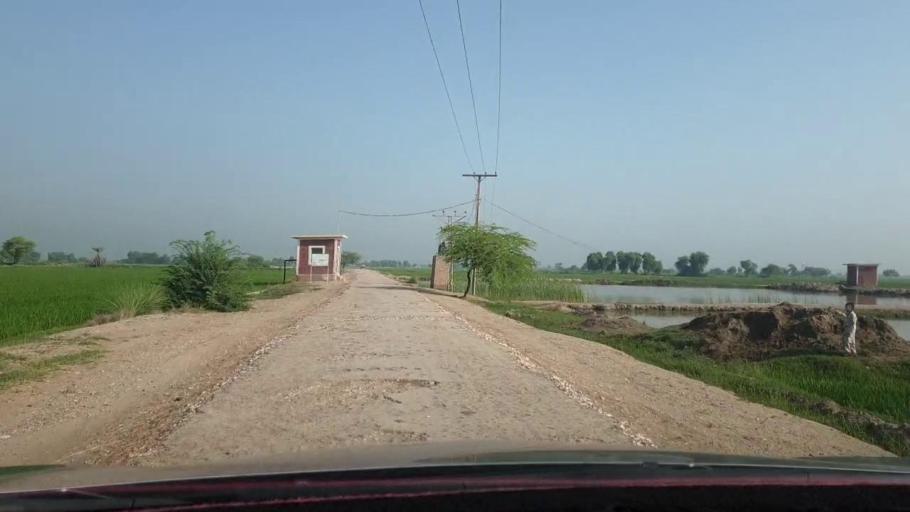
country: PK
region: Sindh
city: Nasirabad
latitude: 27.4268
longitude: 67.9219
